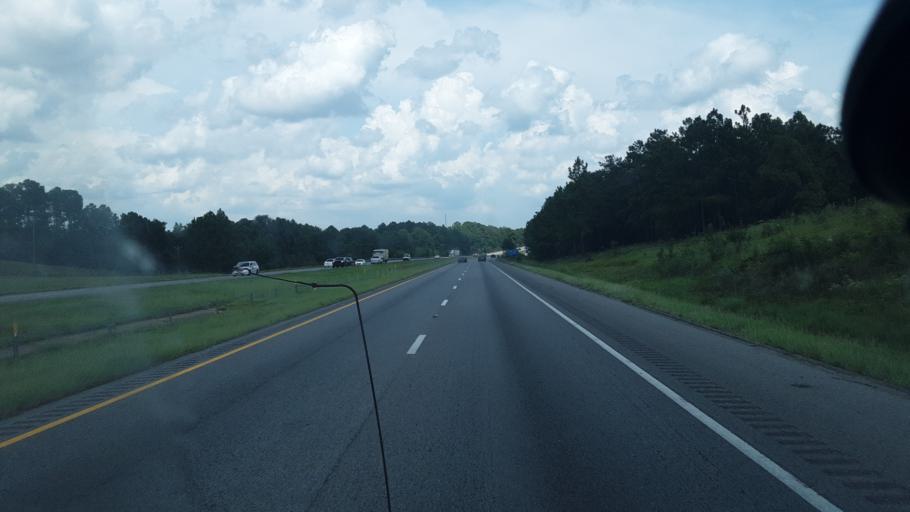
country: US
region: South Carolina
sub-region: Kershaw County
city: Lugoff
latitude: 34.1825
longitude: -80.6981
